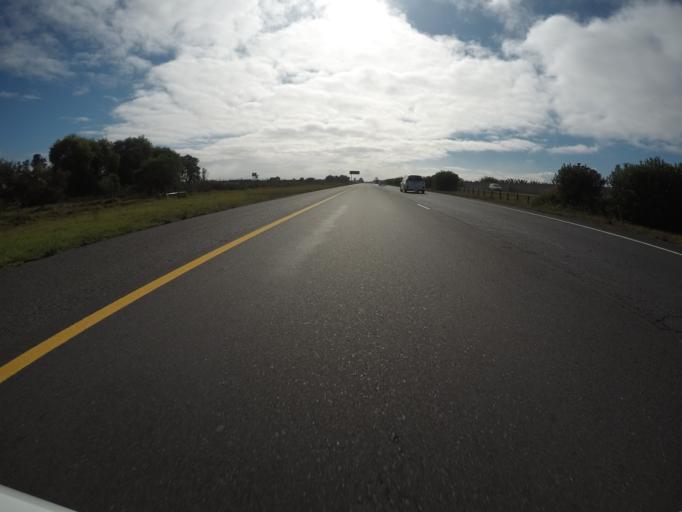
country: ZA
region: Western Cape
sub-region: City of Cape Town
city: Kraaifontein
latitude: -33.8309
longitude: 18.7516
